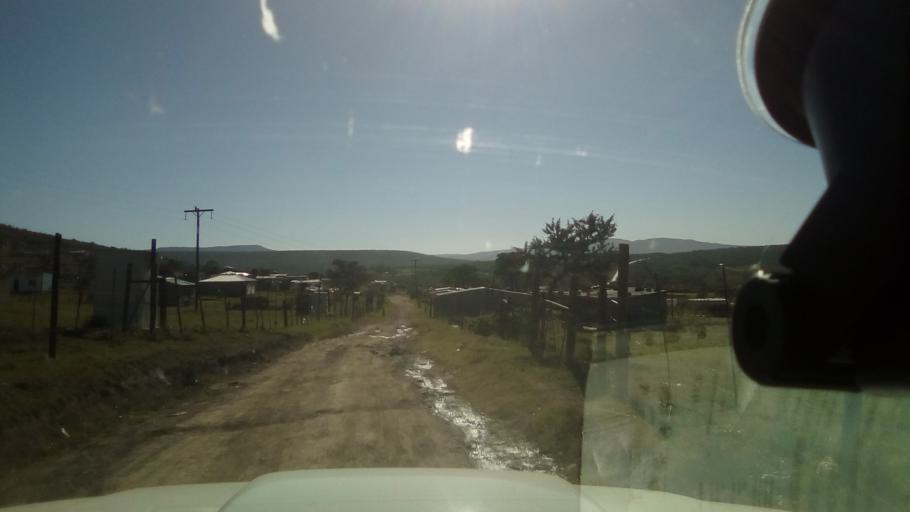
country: ZA
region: Eastern Cape
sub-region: Buffalo City Metropolitan Municipality
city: Bhisho
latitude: -32.8086
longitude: 27.3698
